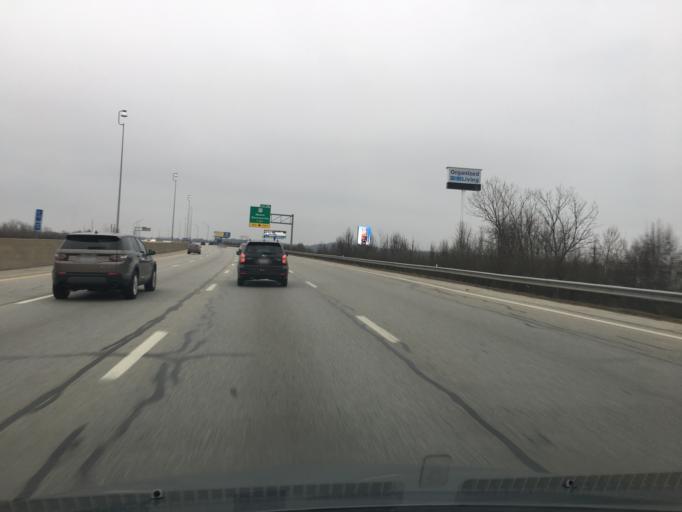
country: US
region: Ohio
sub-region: Hamilton County
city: Sharonville
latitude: 39.2849
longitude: -84.4205
